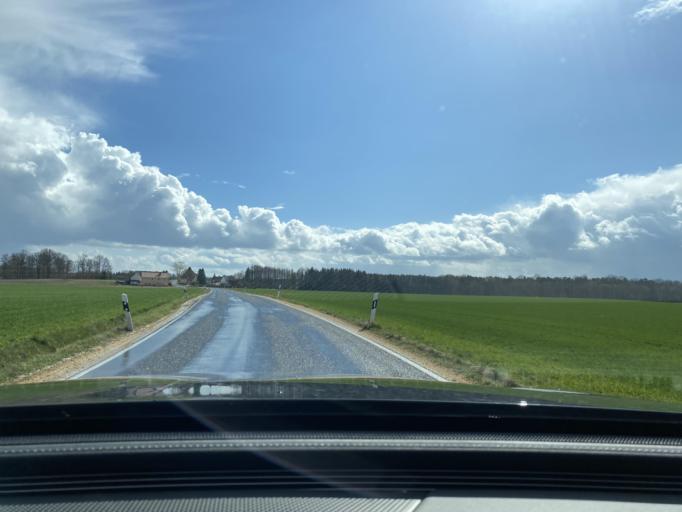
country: DE
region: Saxony
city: Radibor
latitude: 51.2661
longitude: 14.4288
